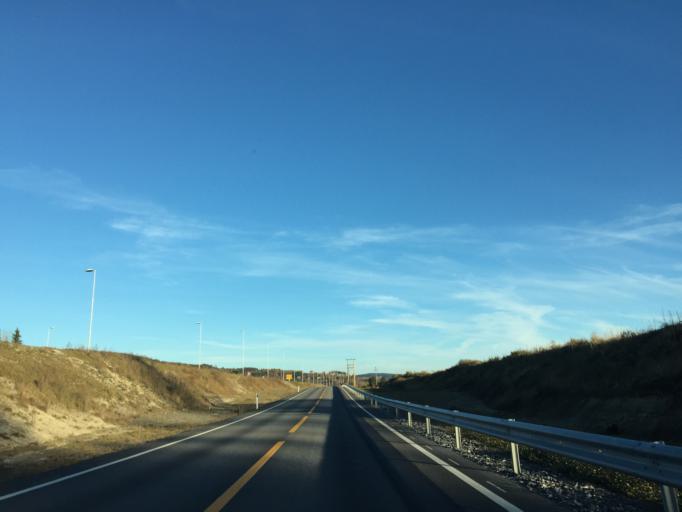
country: NO
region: Hedmark
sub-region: Sor-Odal
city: Skarnes
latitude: 60.2464
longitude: 11.7472
